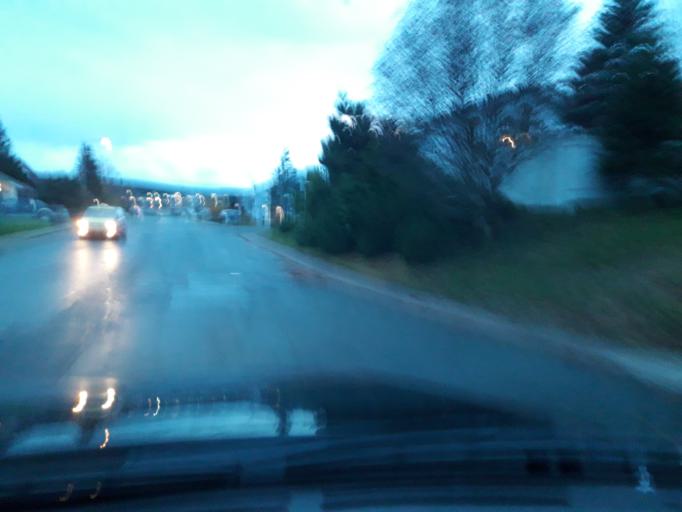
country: CA
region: Newfoundland and Labrador
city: St. John's
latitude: 47.5657
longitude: -52.7530
